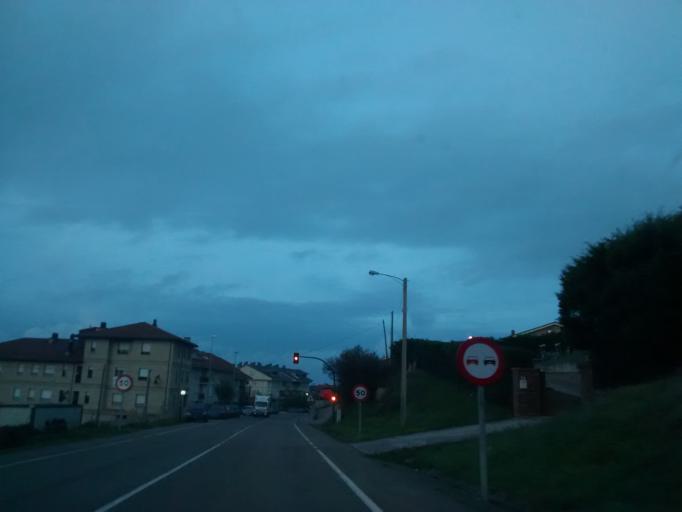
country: ES
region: Cantabria
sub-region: Provincia de Cantabria
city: Santa Cruz de Bezana
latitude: 43.4568
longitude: -3.9324
